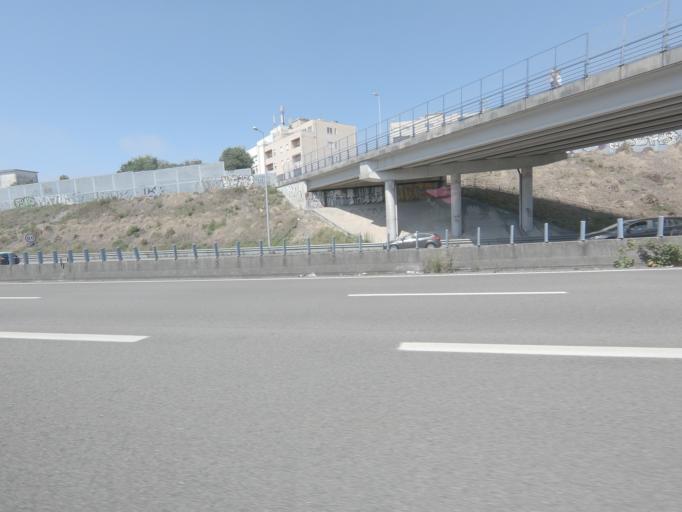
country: PT
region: Porto
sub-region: Matosinhos
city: Guifoes
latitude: 41.1912
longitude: -8.6667
